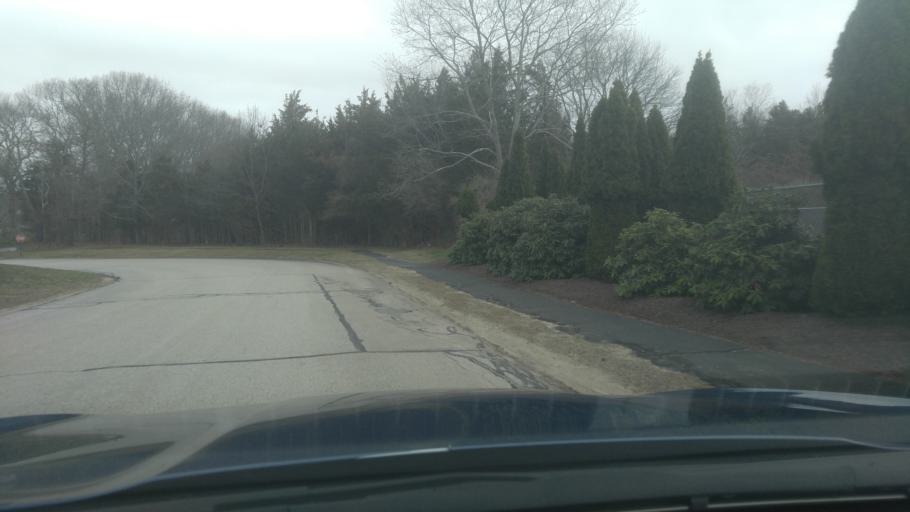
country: US
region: Rhode Island
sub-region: Washington County
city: North Kingstown
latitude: 41.5896
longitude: -71.4451
